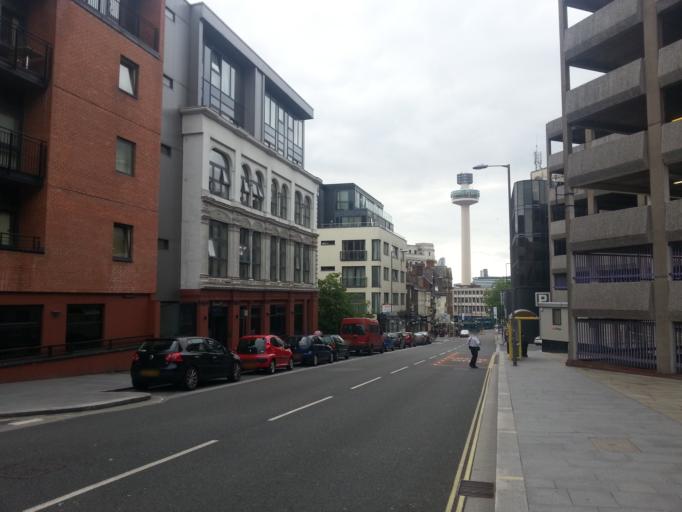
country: GB
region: England
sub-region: Liverpool
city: Liverpool
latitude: 53.4044
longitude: -2.9754
